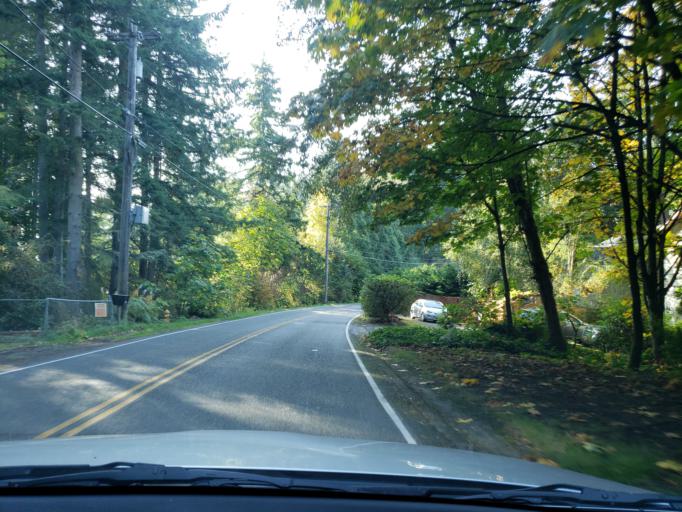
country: US
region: Washington
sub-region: Snohomish County
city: Meadowdale
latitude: 47.8625
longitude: -122.3230
